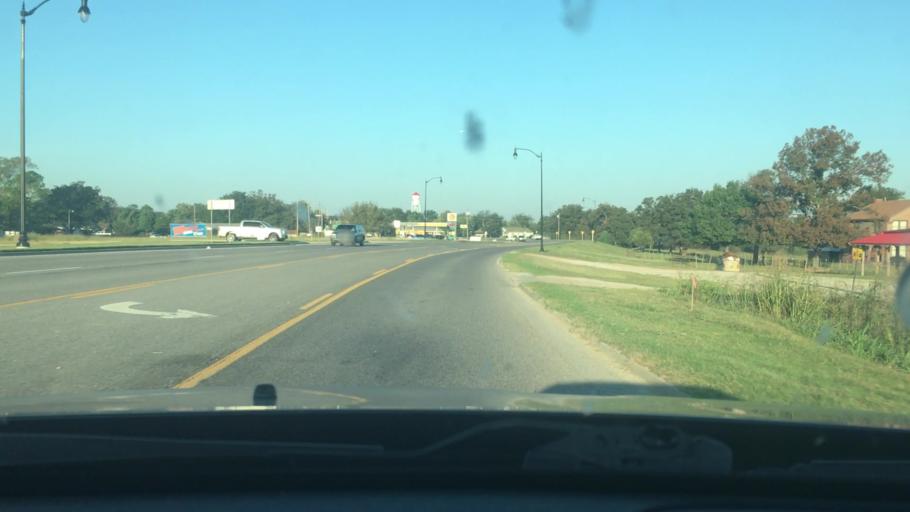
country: US
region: Oklahoma
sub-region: Murray County
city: Davis
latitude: 34.5066
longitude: -97.1075
